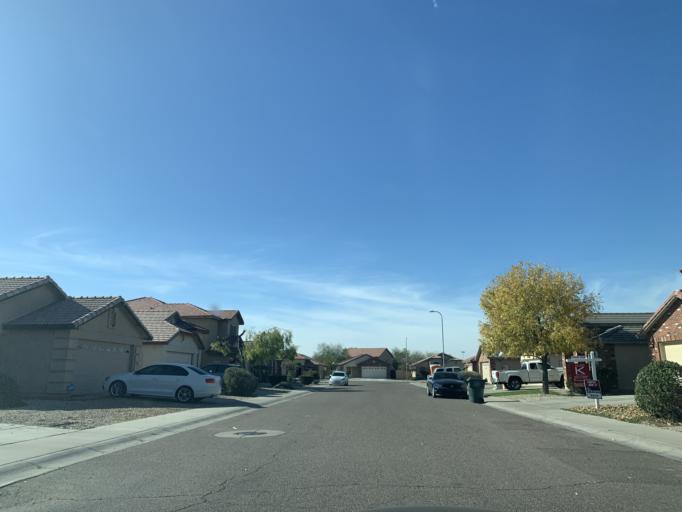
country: US
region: Arizona
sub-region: Maricopa County
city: Laveen
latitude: 33.3981
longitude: -112.1210
